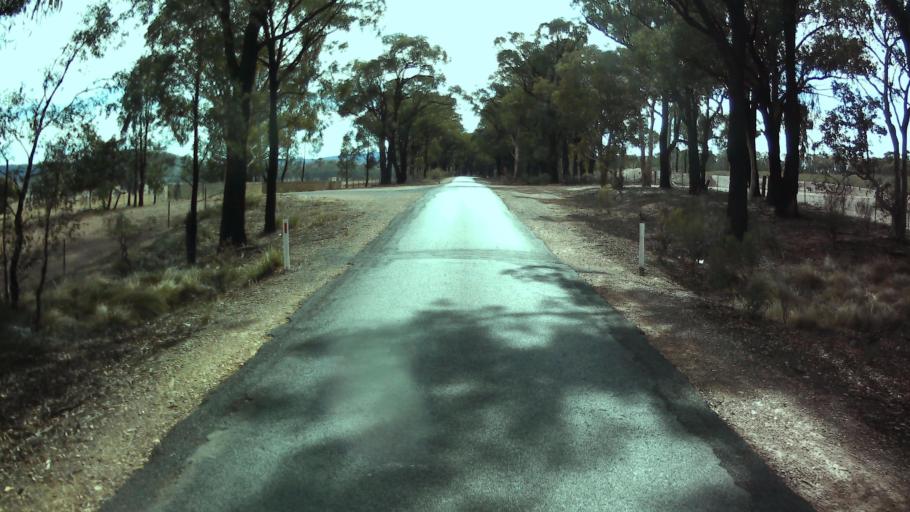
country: AU
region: New South Wales
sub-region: Weddin
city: Grenfell
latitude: -33.8501
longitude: 148.2244
